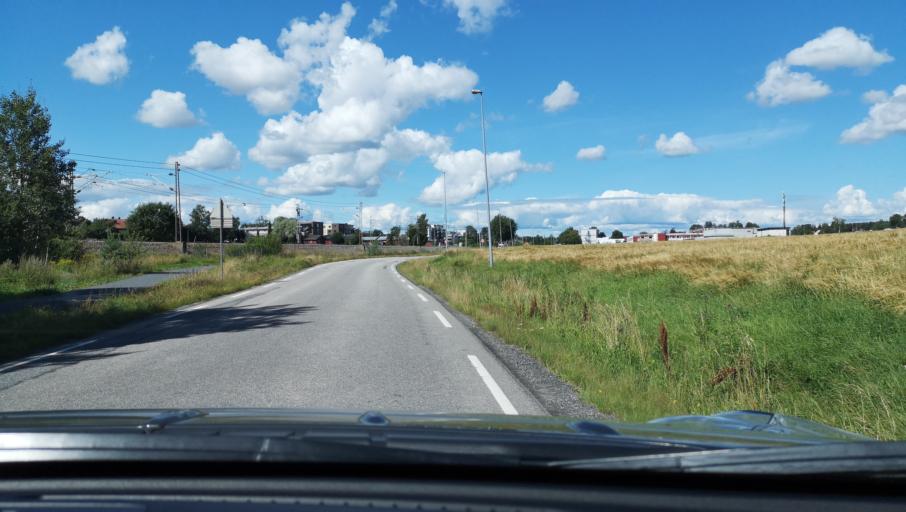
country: NO
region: Akershus
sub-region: As
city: As
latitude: 59.6580
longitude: 10.7982
